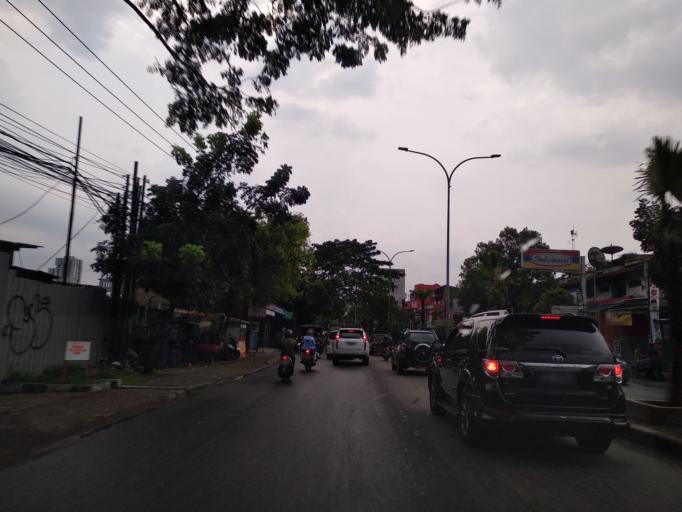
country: ID
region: West Java
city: Bandung
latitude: -6.9588
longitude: 107.6394
